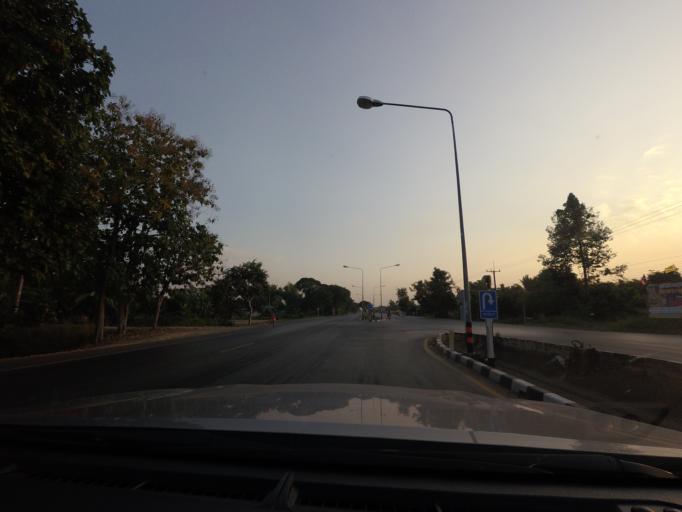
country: TH
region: Phitsanulok
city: Wang Thong
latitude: 16.7306
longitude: 100.4316
